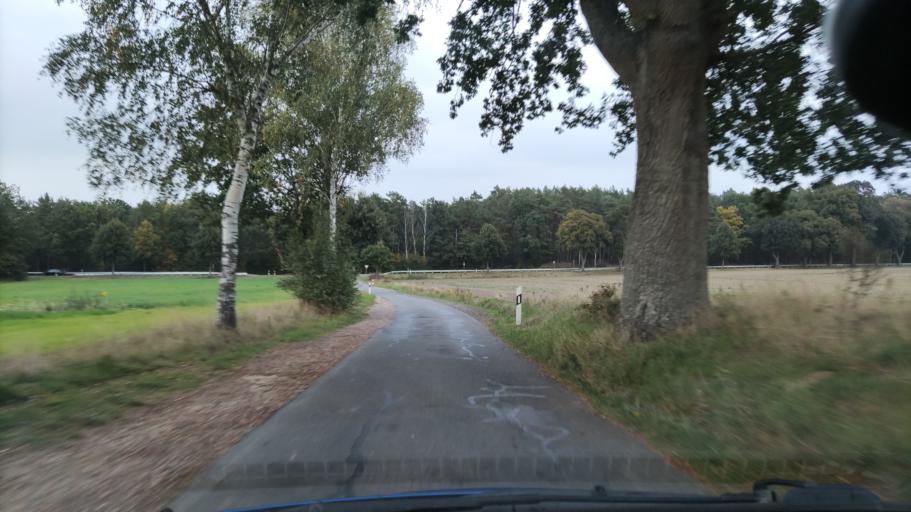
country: DE
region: Lower Saxony
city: Karwitz
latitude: 53.1067
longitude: 11.0206
